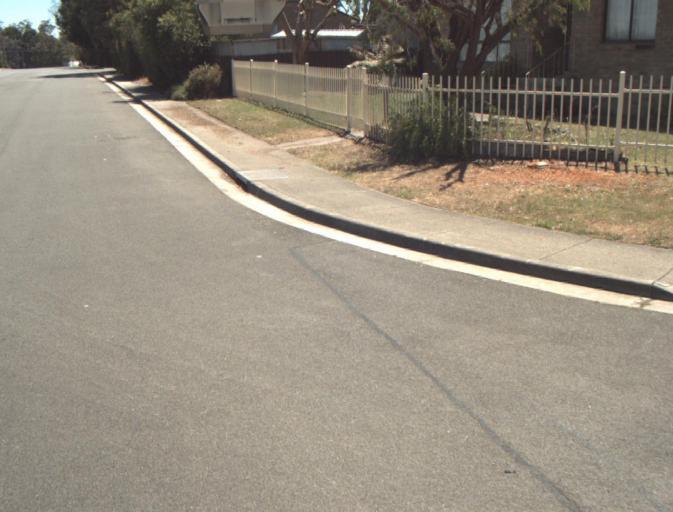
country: AU
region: Tasmania
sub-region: Launceston
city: Mayfield
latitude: -41.3774
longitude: 147.1349
